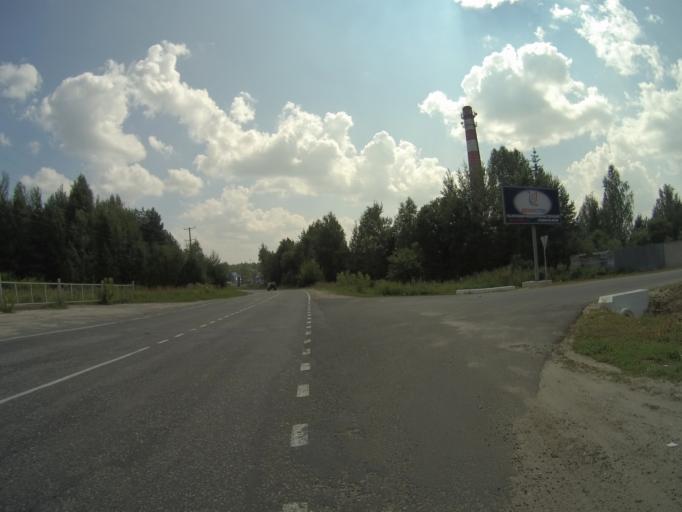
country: RU
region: Vladimir
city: Gus'-Khrustal'nyy
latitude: 55.6385
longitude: 40.7095
